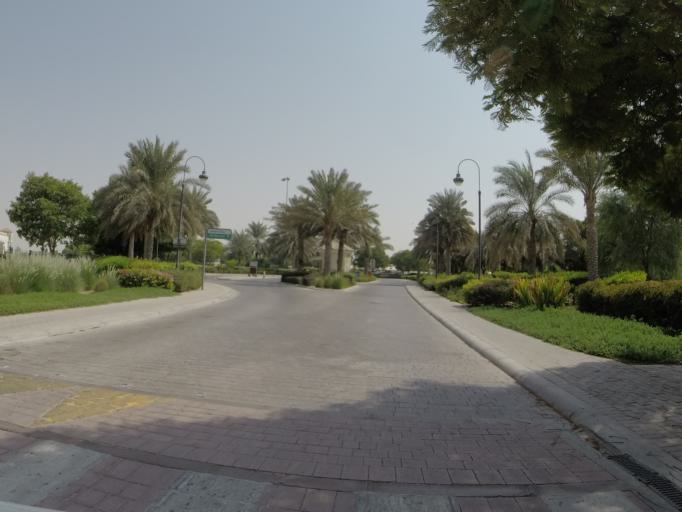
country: AE
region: Dubai
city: Dubai
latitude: 25.0324
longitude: 55.2190
